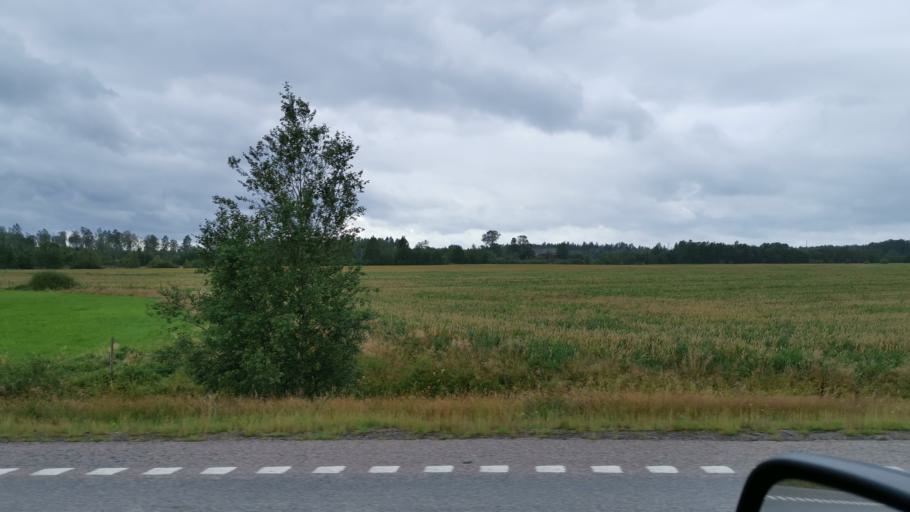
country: SE
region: Vaestra Goetaland
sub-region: Trollhattan
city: Sjuntorp
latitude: 58.3371
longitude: 12.1245
